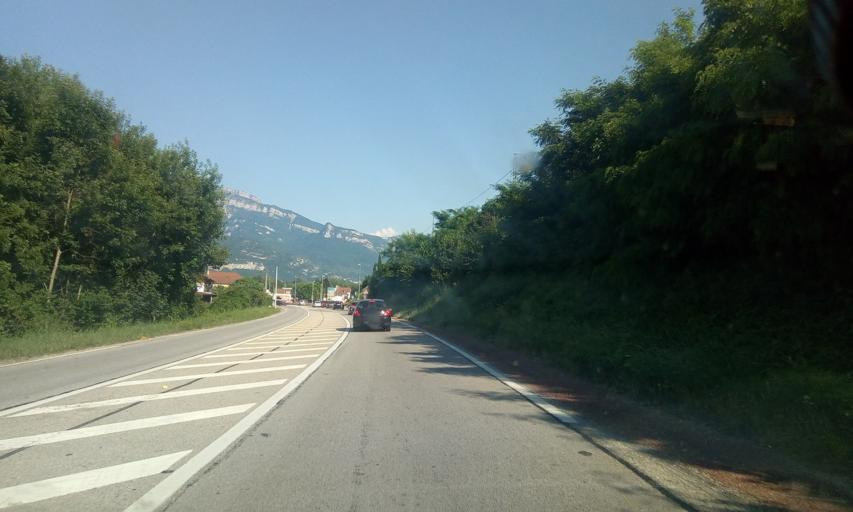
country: FR
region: Rhone-Alpes
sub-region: Departement de l'Isere
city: Moirans
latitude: 45.3278
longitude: 5.5715
